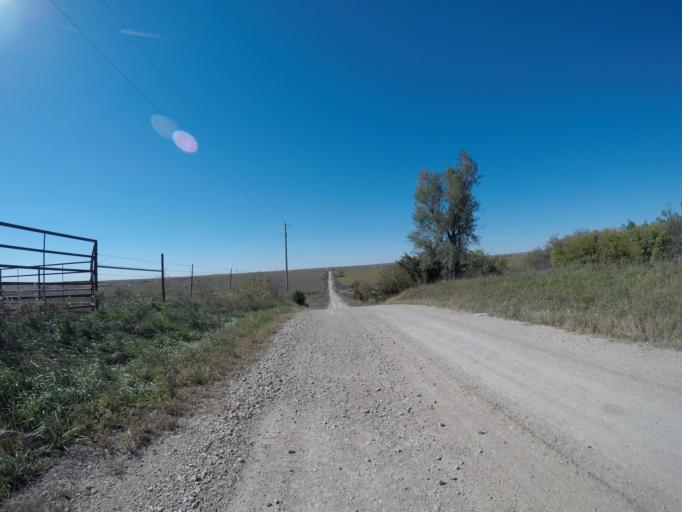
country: US
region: Kansas
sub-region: Wabaunsee County
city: Alma
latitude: 39.0289
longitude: -96.3754
